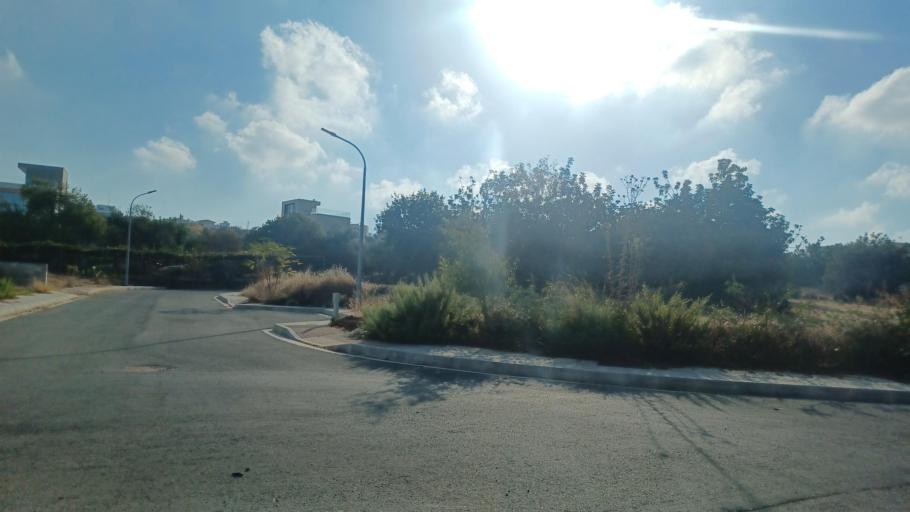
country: CY
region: Pafos
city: Paphos
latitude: 34.7819
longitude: 32.4551
